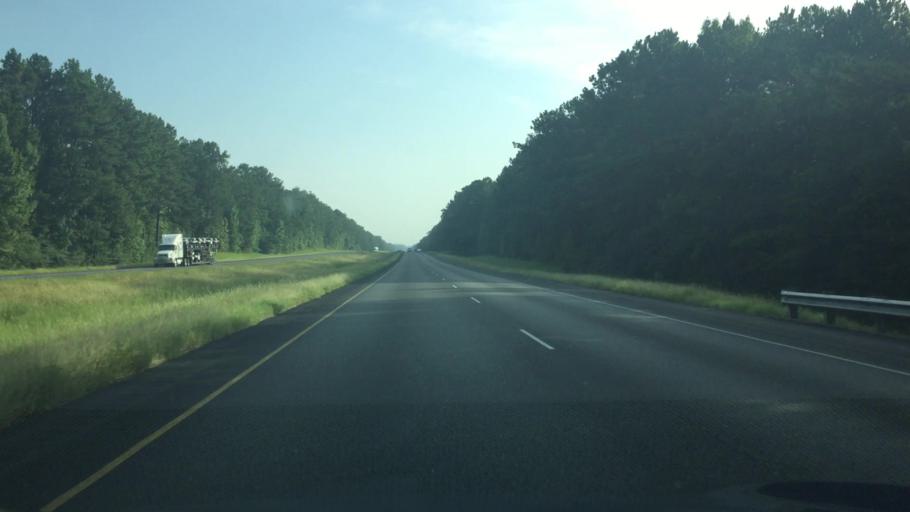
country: US
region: Alabama
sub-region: Butler County
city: Georgiana
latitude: 31.7171
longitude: -86.7290
